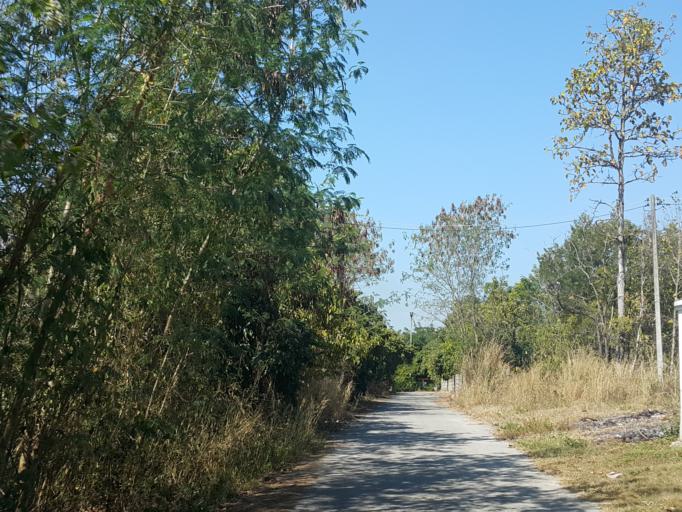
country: TH
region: Chiang Mai
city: Mae Taeng
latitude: 19.0348
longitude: 98.9845
